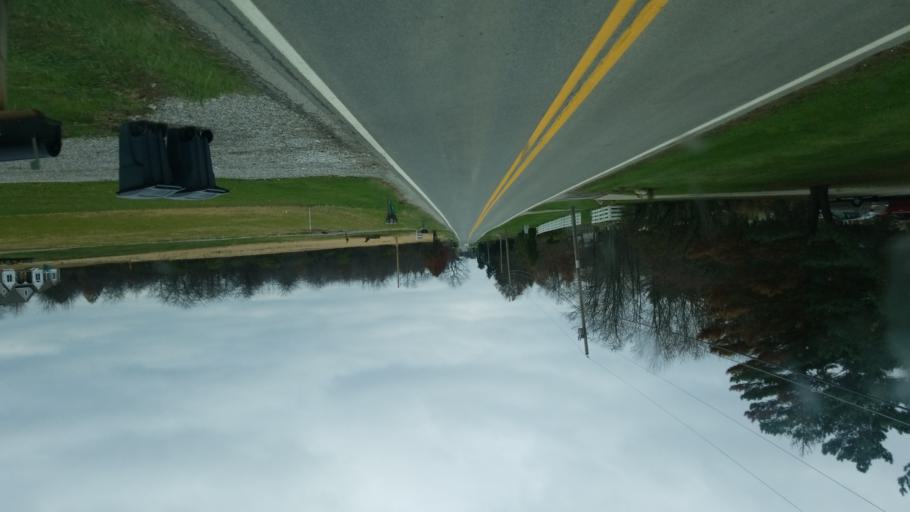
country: US
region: Ohio
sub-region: Franklin County
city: New Albany
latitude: 40.1326
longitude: -82.8152
